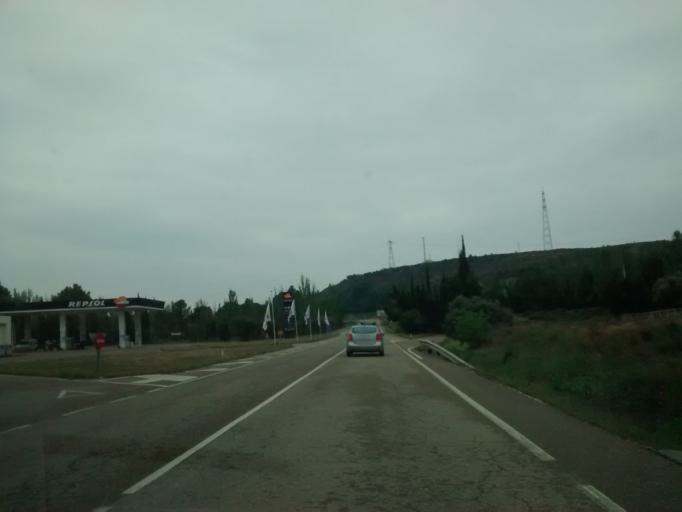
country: ES
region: Aragon
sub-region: Provincia de Zaragoza
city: Caspe
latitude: 41.2497
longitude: -0.0686
